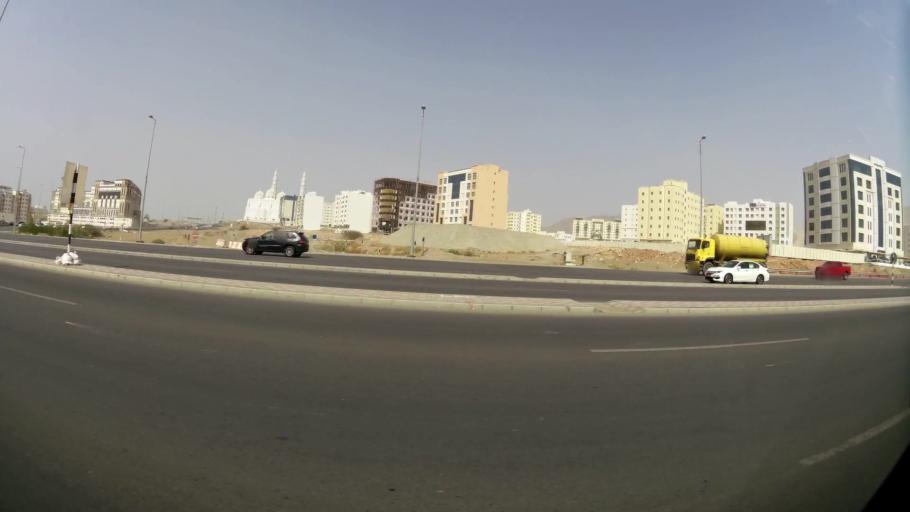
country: OM
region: Muhafazat Masqat
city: Bawshar
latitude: 23.5760
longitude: 58.4077
